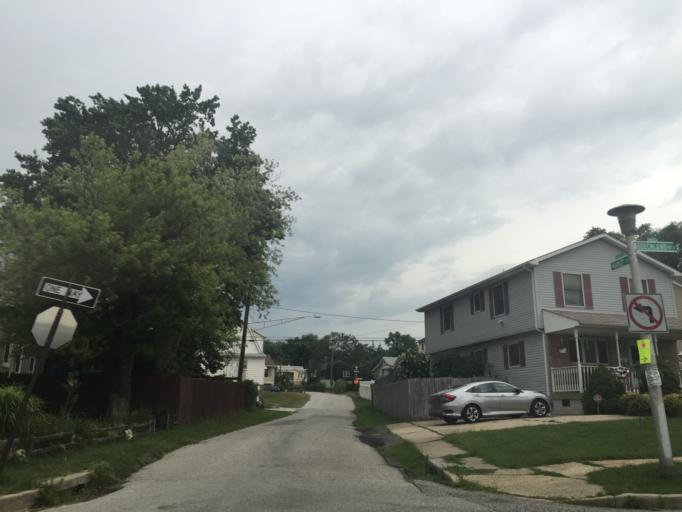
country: US
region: Maryland
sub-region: Baltimore County
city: Parkville
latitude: 39.3590
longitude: -76.5617
